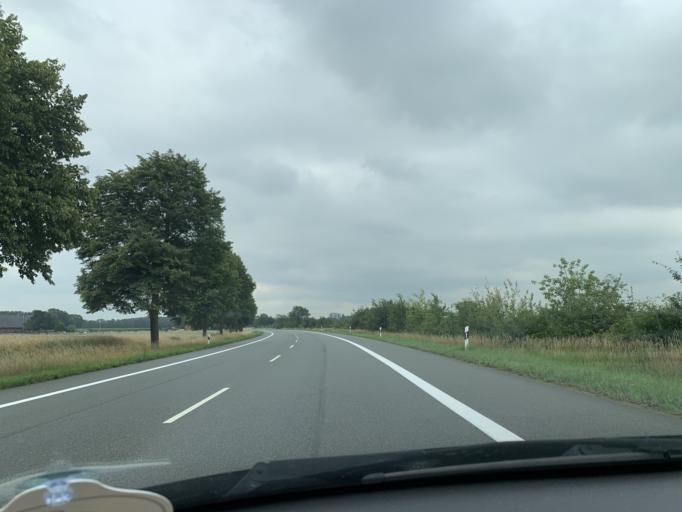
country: DE
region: North Rhine-Westphalia
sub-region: Regierungsbezirk Munster
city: Warendorf
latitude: 51.9303
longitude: 8.0236
